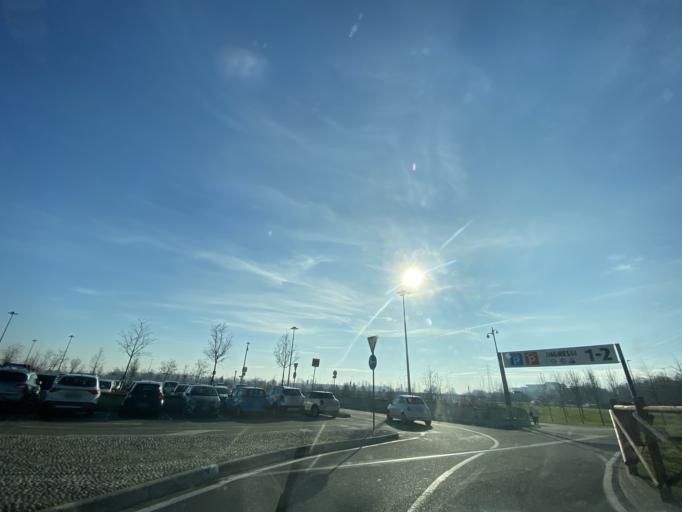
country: IT
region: Lombardy
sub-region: Citta metropolitana di Milano
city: Passirana
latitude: 45.5631
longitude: 9.0480
